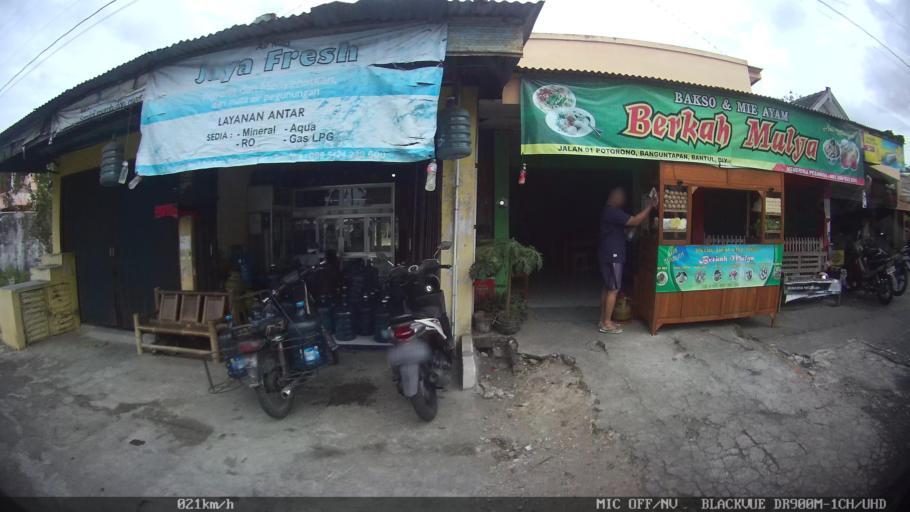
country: ID
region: Daerah Istimewa Yogyakarta
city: Depok
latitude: -7.8336
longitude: 110.4222
